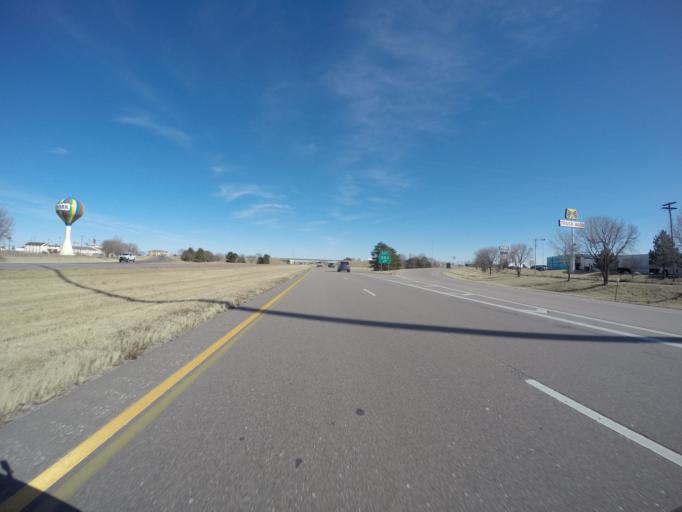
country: US
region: Nebraska
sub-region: York County
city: York
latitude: 40.8211
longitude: -97.6024
